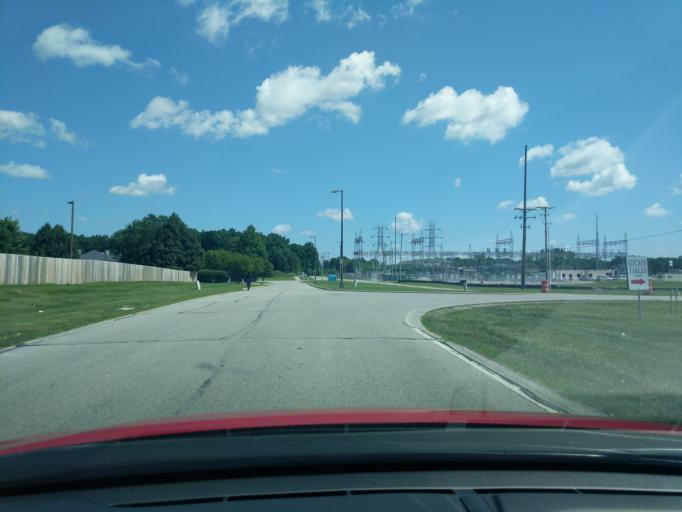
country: US
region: Ohio
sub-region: Franklin County
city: Huber Ridge
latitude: 40.0595
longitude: -82.9083
